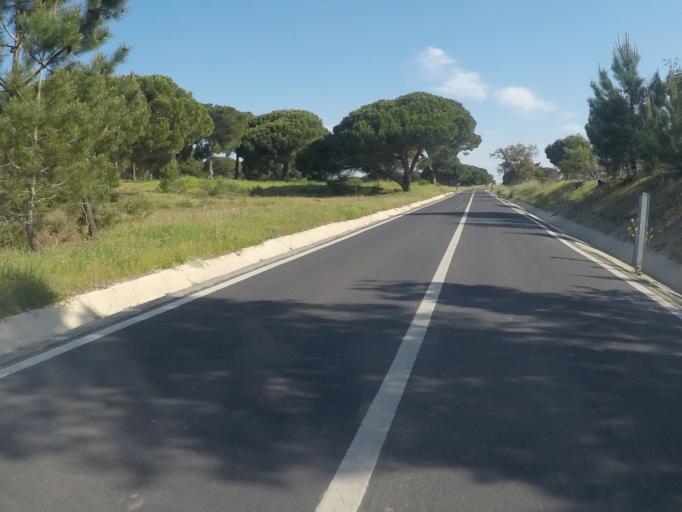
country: PT
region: Setubal
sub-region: Sesimbra
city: Sesimbra
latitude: 38.5114
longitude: -9.1451
